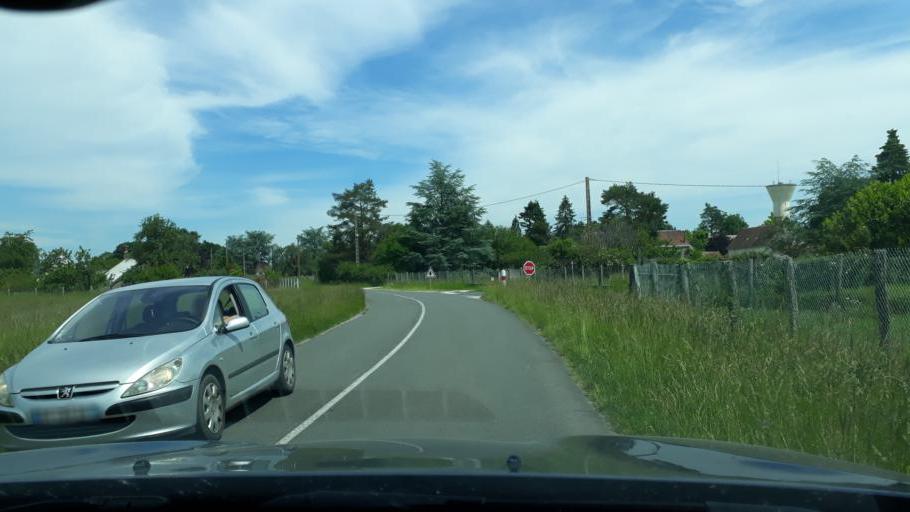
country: FR
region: Centre
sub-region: Departement du Loiret
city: Boiscommun
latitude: 48.0281
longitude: 2.3105
